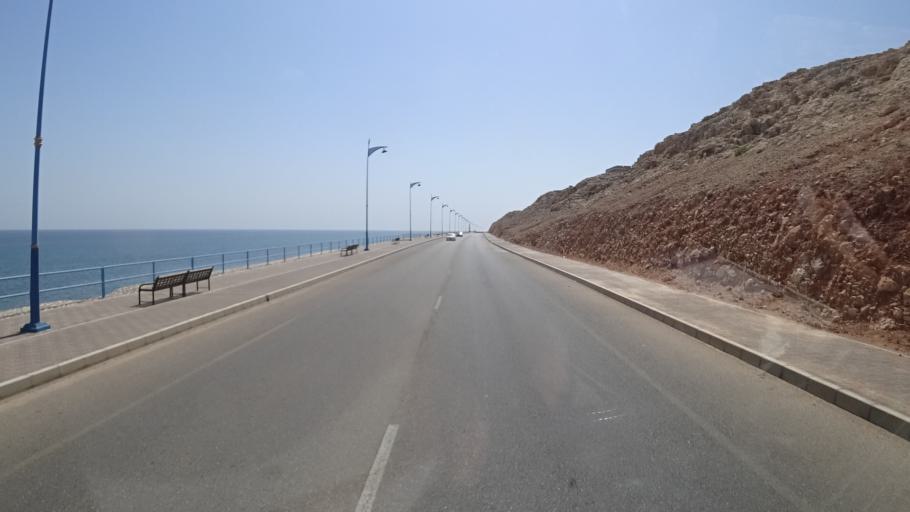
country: OM
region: Ash Sharqiyah
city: Sur
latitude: 22.5662
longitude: 59.5653
